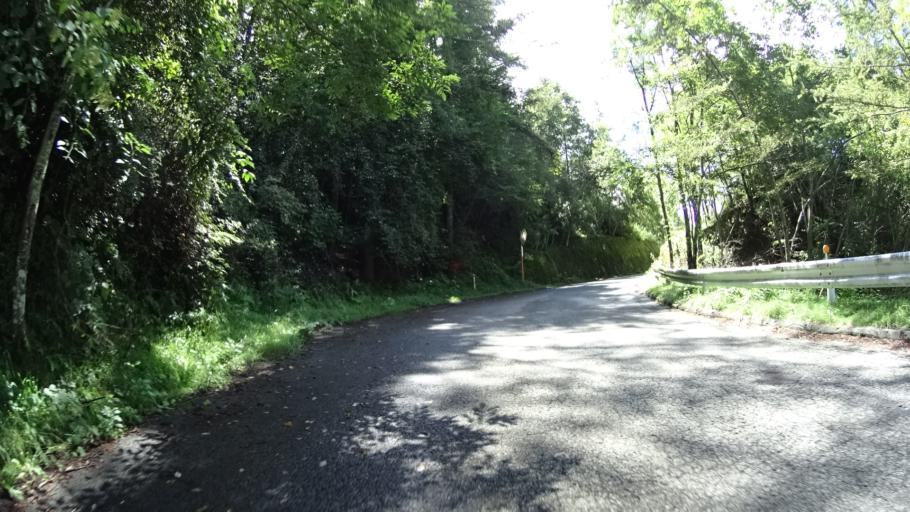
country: JP
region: Yamanashi
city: Enzan
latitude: 35.7202
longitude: 138.8416
